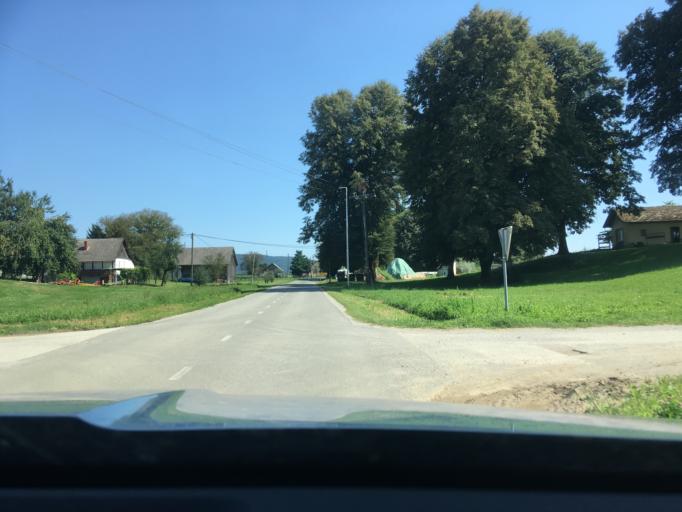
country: SI
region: Metlika
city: Metlika
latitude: 45.5890
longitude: 15.2781
